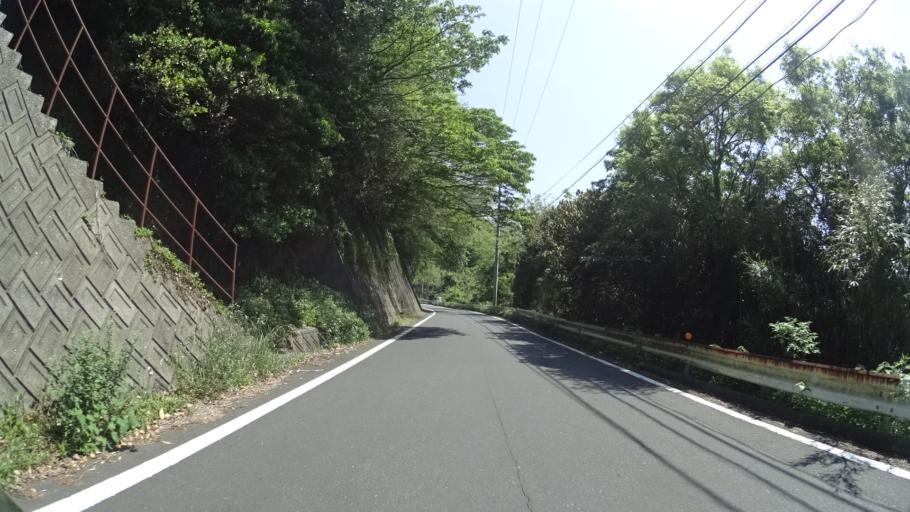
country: JP
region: Ehime
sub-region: Nishiuwa-gun
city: Ikata-cho
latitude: 33.3870
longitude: 132.0888
